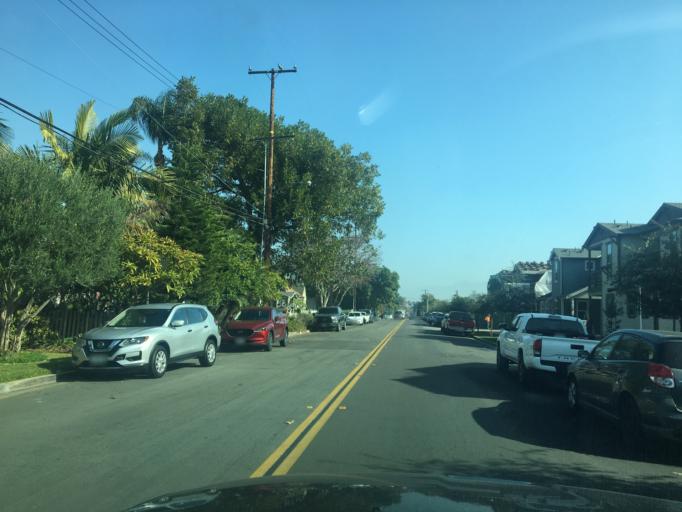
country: US
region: California
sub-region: Orange County
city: Tustin
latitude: 33.7401
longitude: -117.8282
